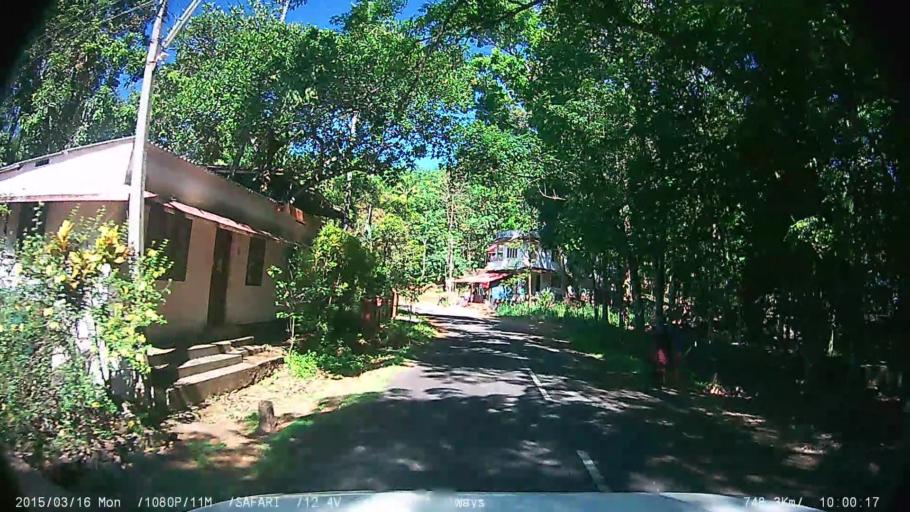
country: IN
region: Kerala
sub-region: Kottayam
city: Palackattumala
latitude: 9.7819
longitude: 76.5902
